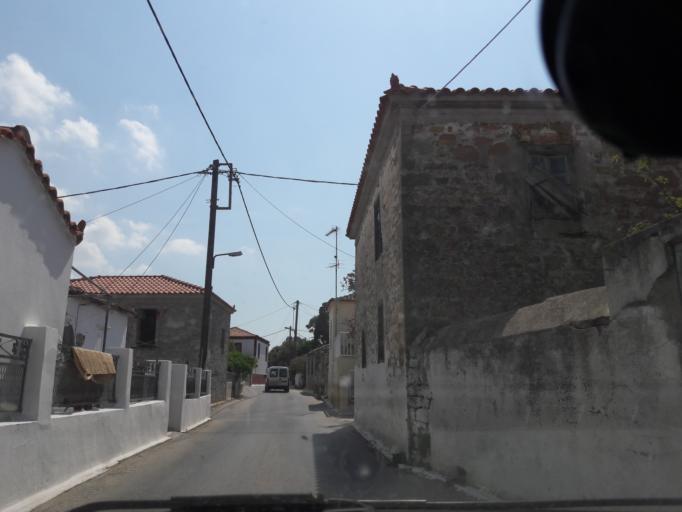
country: GR
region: North Aegean
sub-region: Nomos Lesvou
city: Myrina
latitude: 39.9262
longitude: 25.3325
